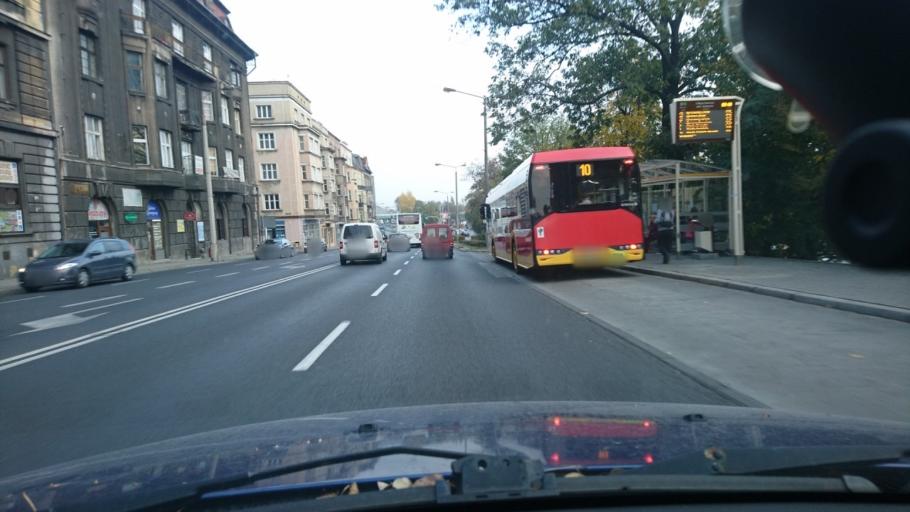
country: PL
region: Silesian Voivodeship
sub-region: Bielsko-Biala
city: Bielsko-Biala
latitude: 49.8279
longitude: 19.0447
